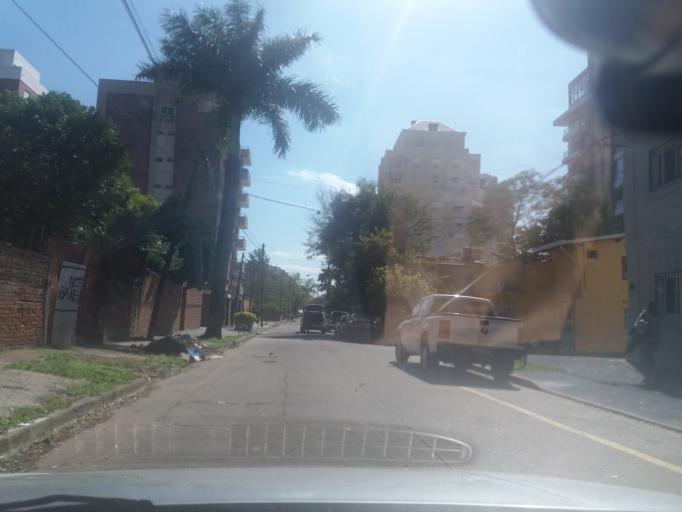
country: AR
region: Corrientes
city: Corrientes
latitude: -27.4684
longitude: -58.8507
